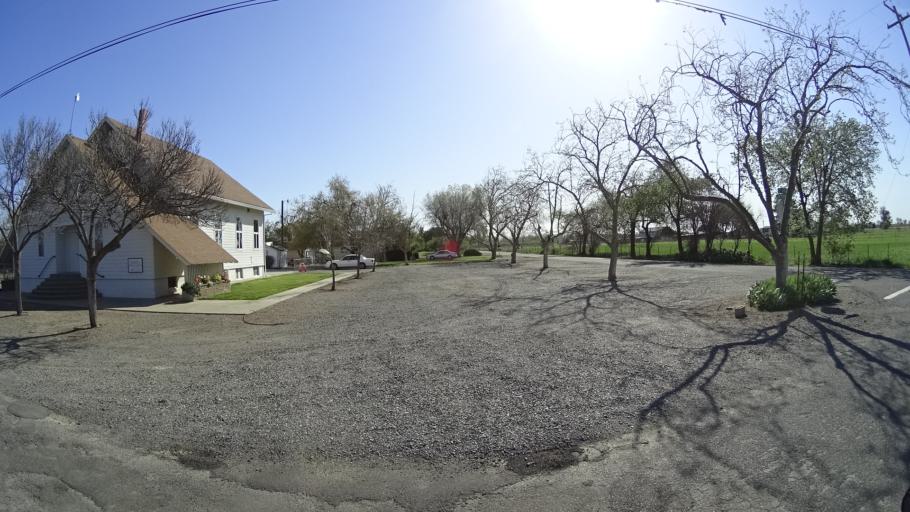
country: US
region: California
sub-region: Glenn County
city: Hamilton City
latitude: 39.7971
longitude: -122.0665
